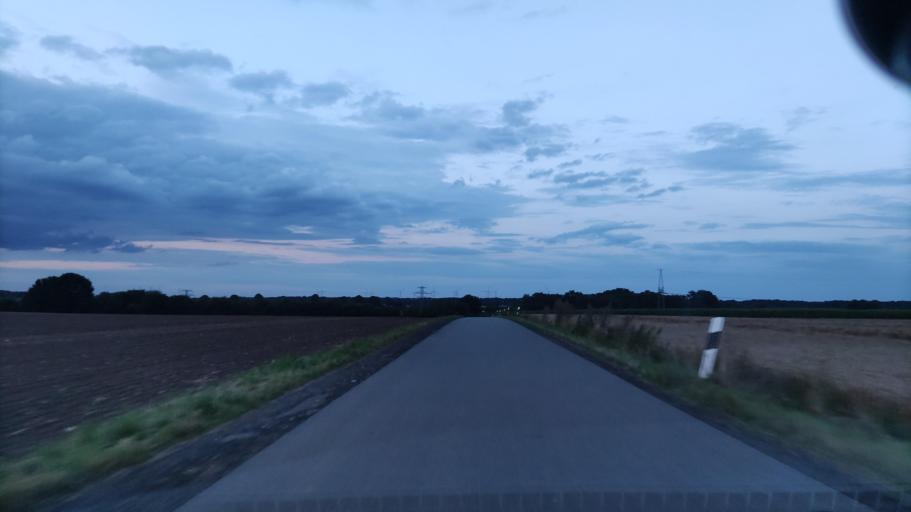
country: DE
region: Schleswig-Holstein
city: Kruzen
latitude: 53.3936
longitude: 10.5186
